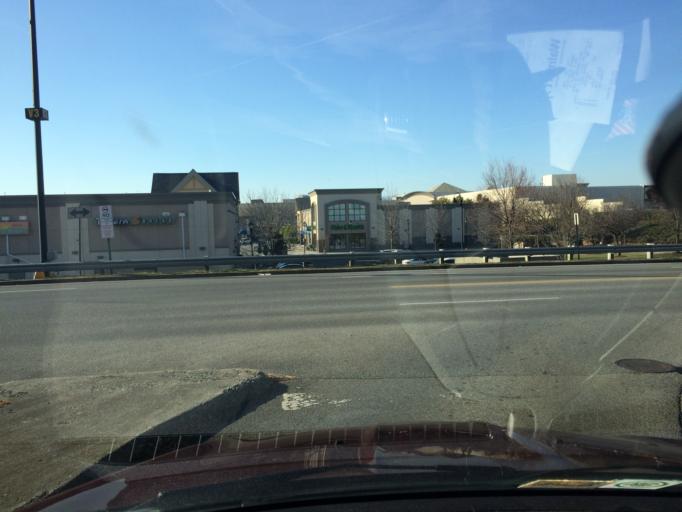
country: US
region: Virginia
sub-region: Roanoke County
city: Hollins
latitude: 37.3057
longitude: -79.9620
